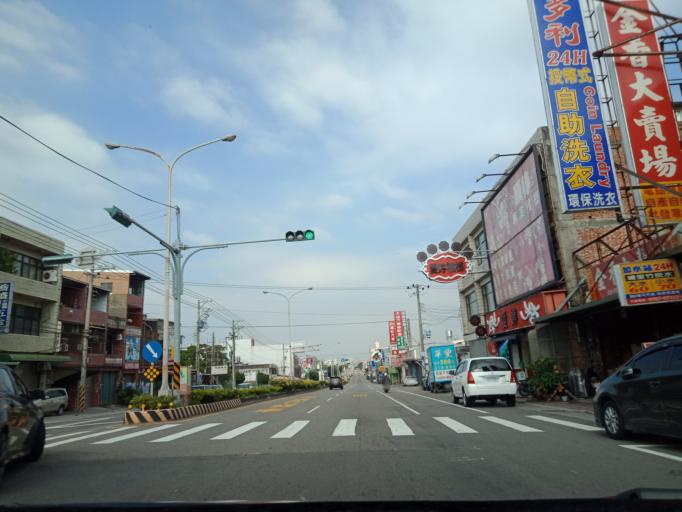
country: TW
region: Taiwan
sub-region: Hsinchu
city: Zhubei
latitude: 24.8809
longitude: 121.0084
